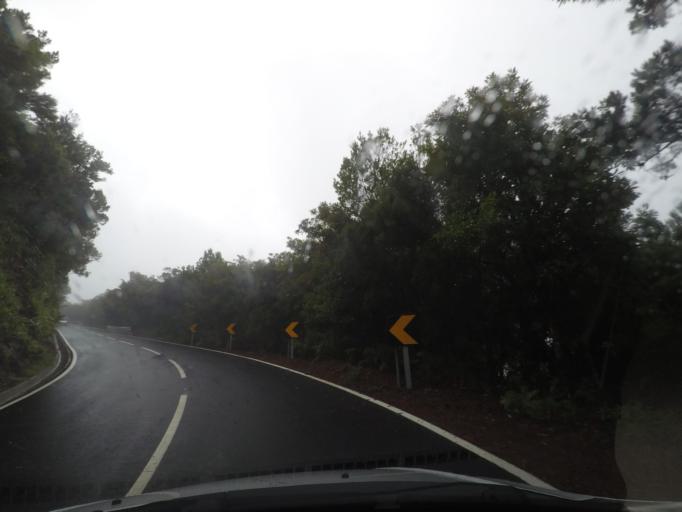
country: PT
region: Madeira
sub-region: Santana
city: Santana
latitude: 32.7747
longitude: -16.9062
